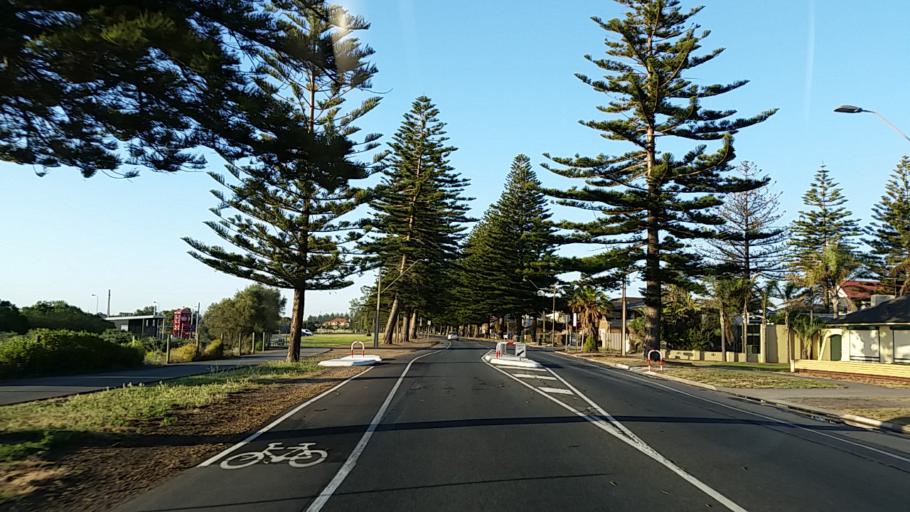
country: AU
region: South Australia
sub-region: Port Adelaide Enfield
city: Birkenhead
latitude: -34.8018
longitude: 138.4918
